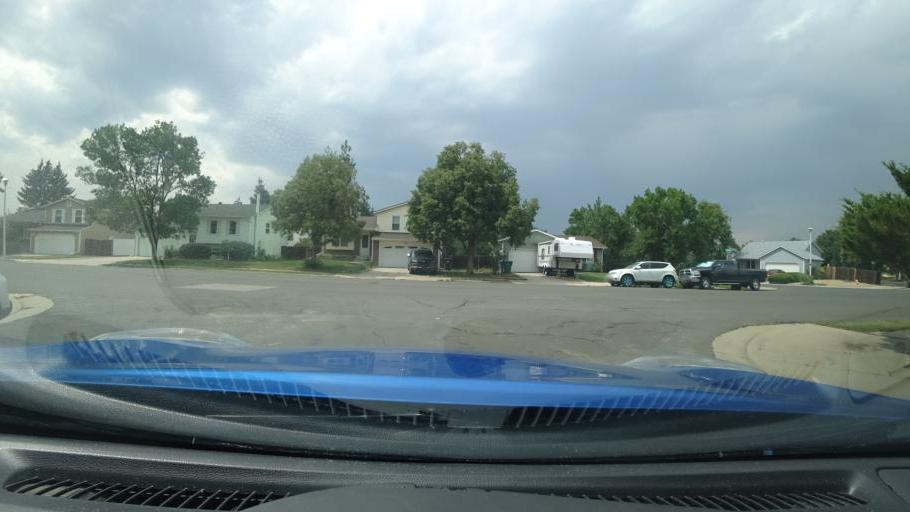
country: US
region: Colorado
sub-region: Adams County
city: Aurora
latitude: 39.6842
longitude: -104.7595
